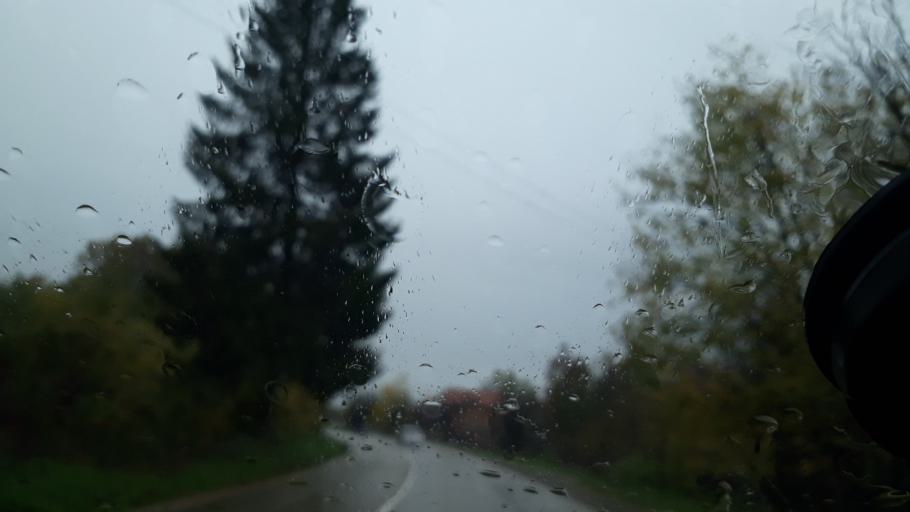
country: BA
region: Republika Srpska
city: Maglajani
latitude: 44.8641
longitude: 17.4332
